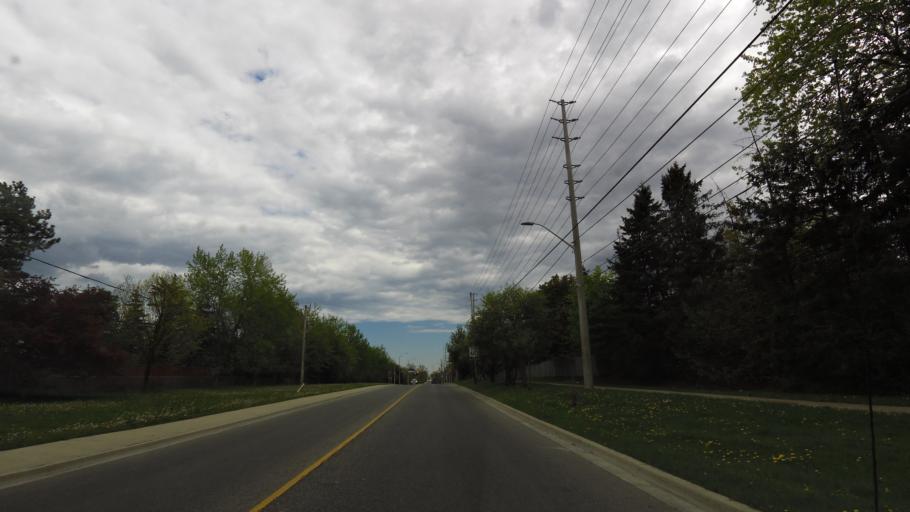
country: CA
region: Ontario
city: Mississauga
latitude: 43.6053
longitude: -79.7225
